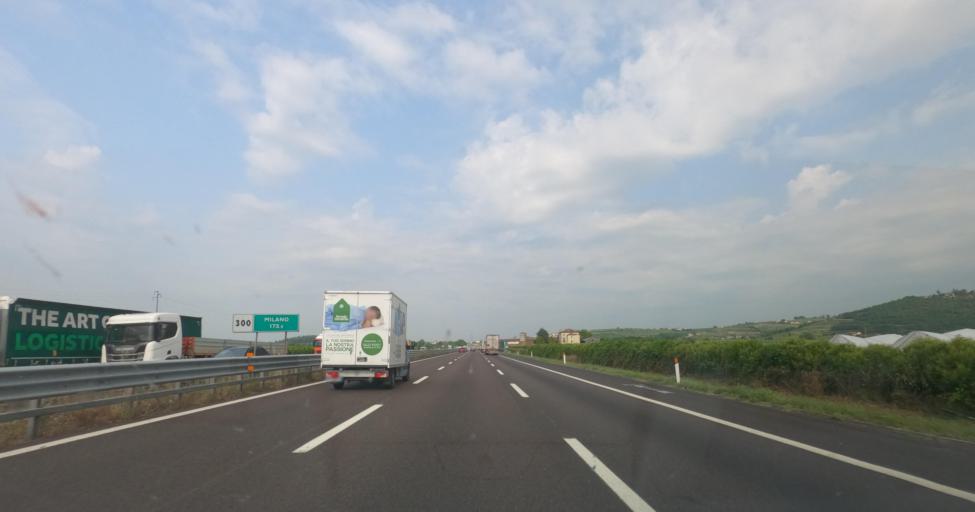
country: IT
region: Veneto
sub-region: Provincia di Verona
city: Belfiore
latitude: 45.4131
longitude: 11.2137
